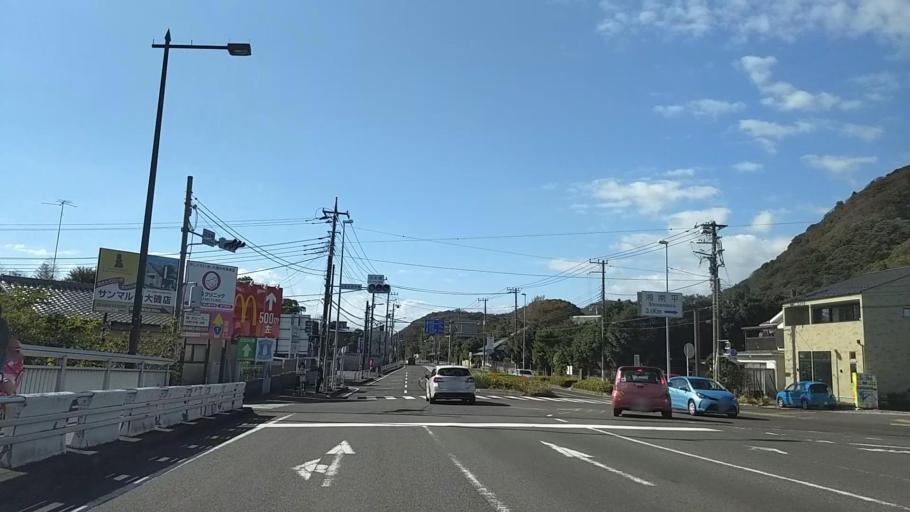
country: JP
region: Kanagawa
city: Hiratsuka
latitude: 35.3227
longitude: 139.3283
